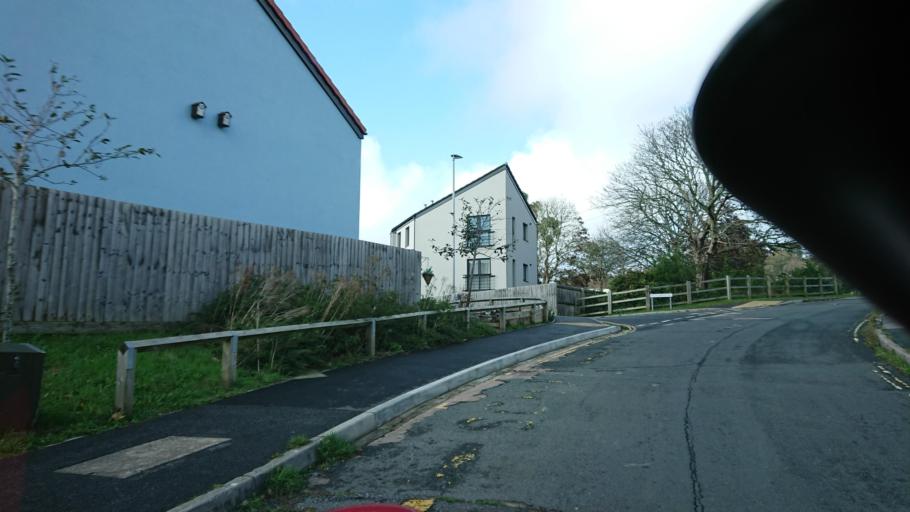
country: GB
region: England
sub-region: Plymouth
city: Plymouth
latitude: 50.4179
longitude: -4.1563
